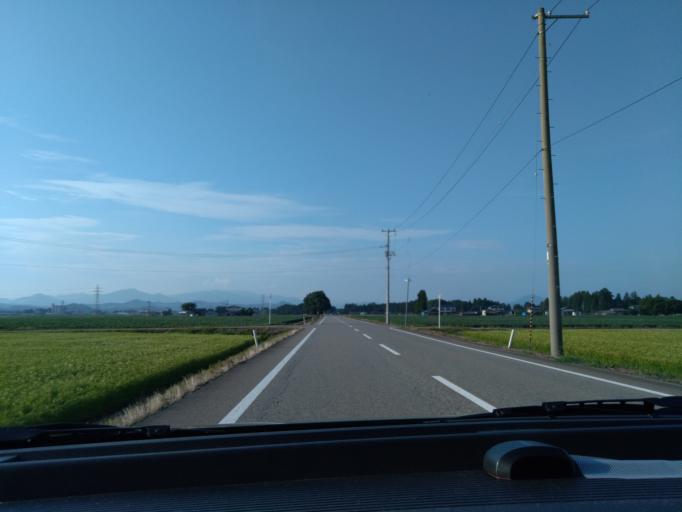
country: JP
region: Akita
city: Kakunodatemachi
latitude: 39.5313
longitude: 140.5583
